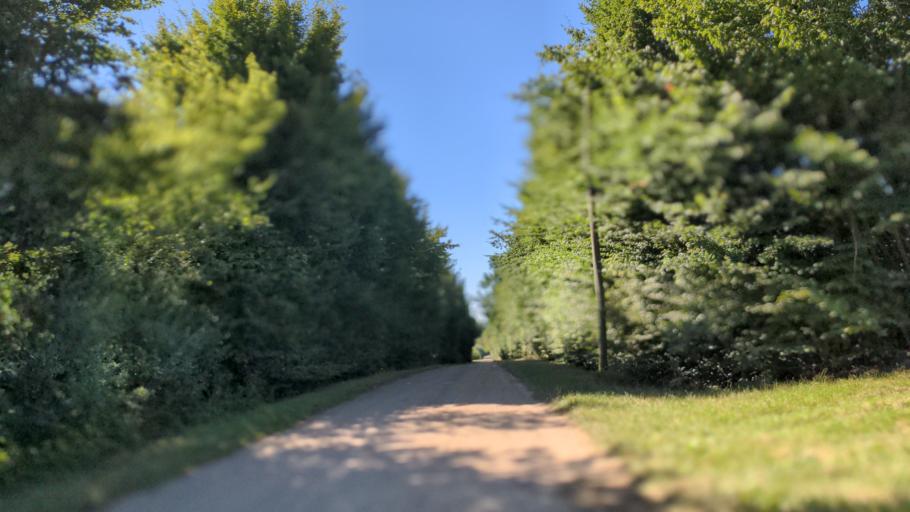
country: DE
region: Mecklenburg-Vorpommern
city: Selmsdorf
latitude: 53.8390
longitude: 10.8539
